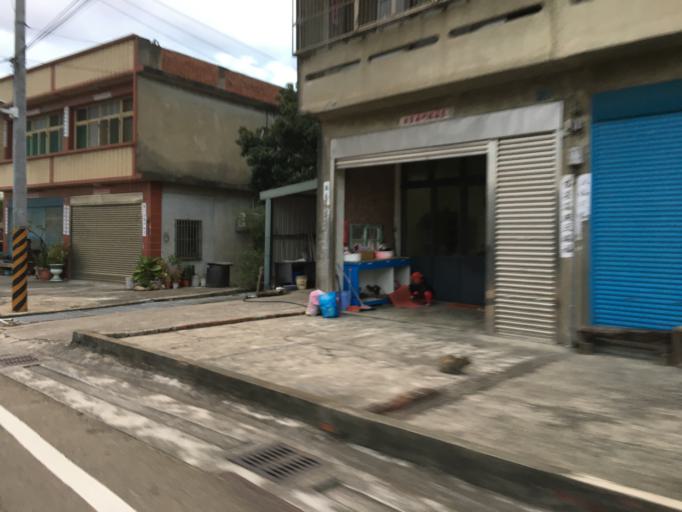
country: TW
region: Taiwan
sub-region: Hsinchu
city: Hsinchu
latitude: 24.7299
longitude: 120.8778
